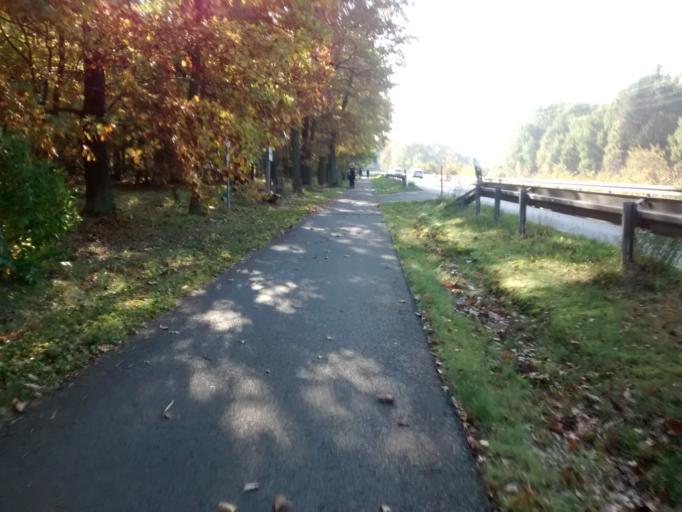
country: DE
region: Brandenburg
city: Hennigsdorf
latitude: 52.6441
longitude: 13.2282
